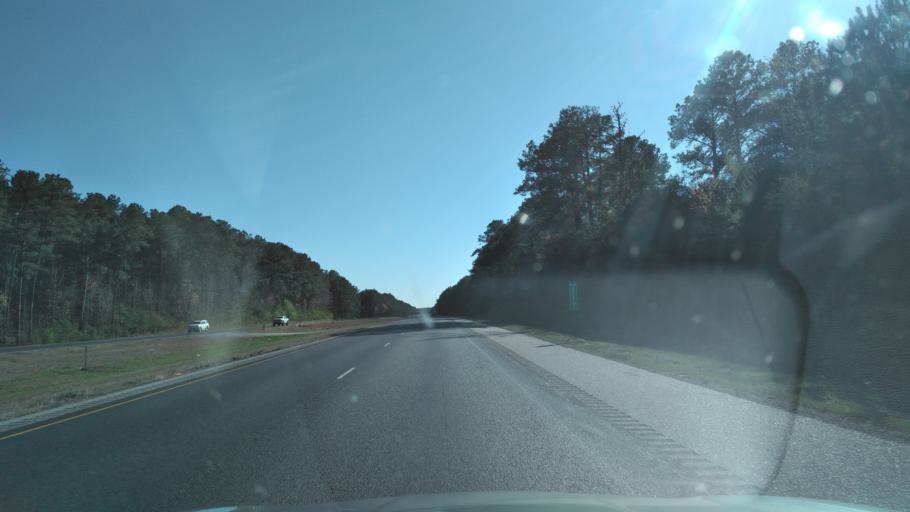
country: US
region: Alabama
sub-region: Butler County
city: Georgiana
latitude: 31.6889
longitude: -86.7490
